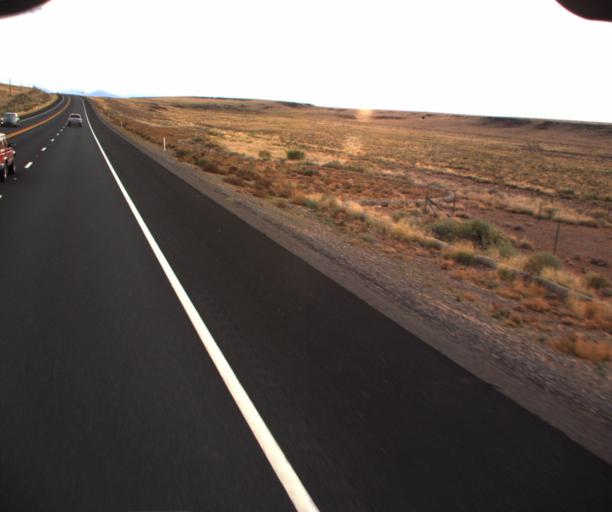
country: US
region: Arizona
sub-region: Coconino County
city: Tuba City
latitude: 35.7073
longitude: -111.4944
